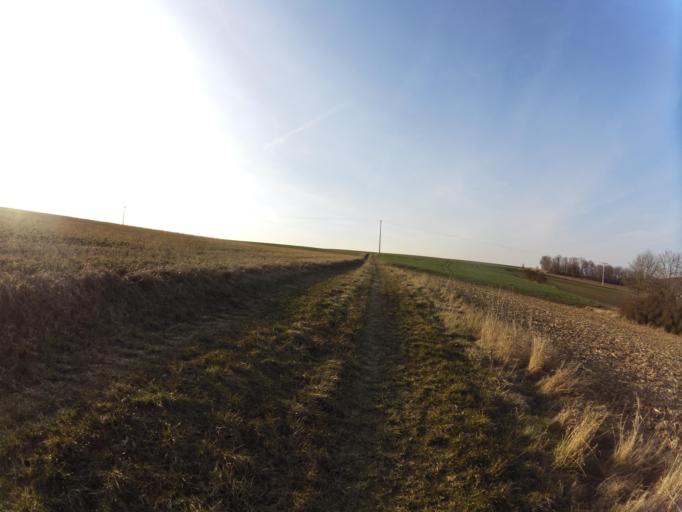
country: DE
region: Bavaria
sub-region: Regierungsbezirk Unterfranken
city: Prosselsheim
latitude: 49.8352
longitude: 10.1436
